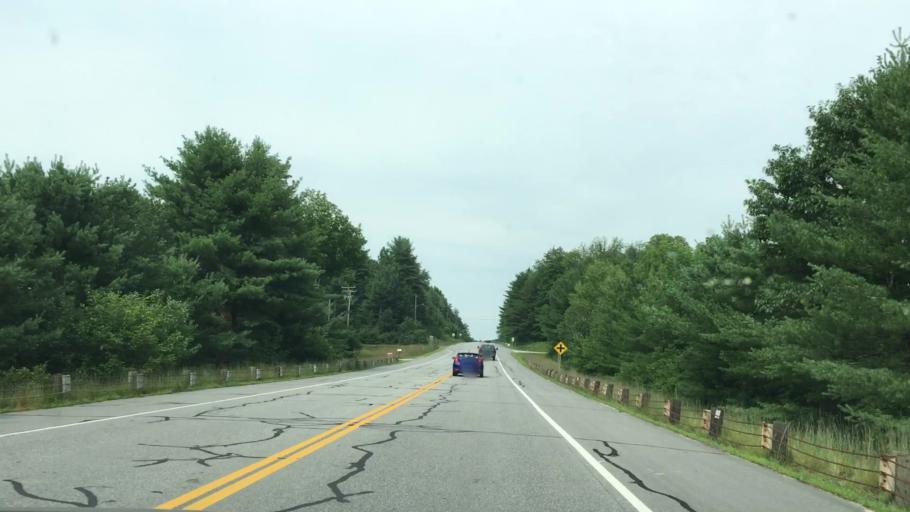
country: US
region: New Hampshire
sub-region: Hillsborough County
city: Antrim
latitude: 43.0508
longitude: -71.9258
